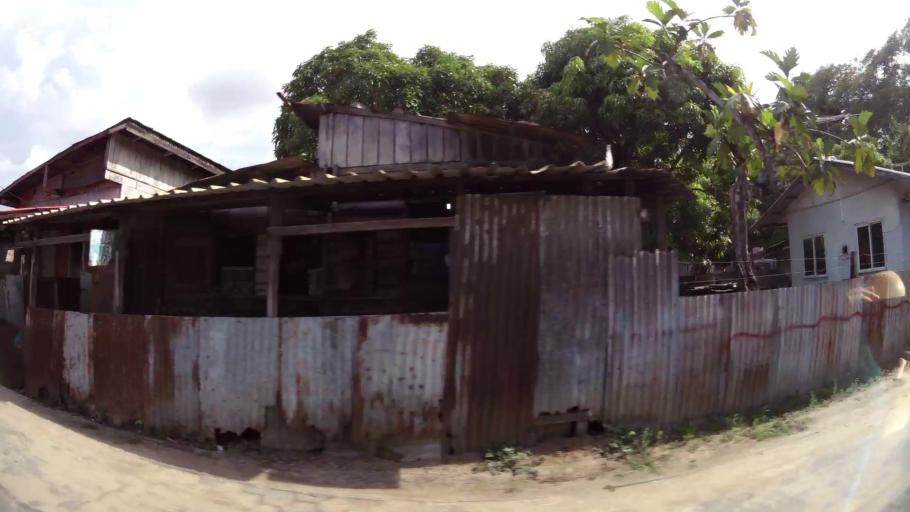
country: SR
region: Paramaribo
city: Paramaribo
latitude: 5.8408
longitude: -55.1567
